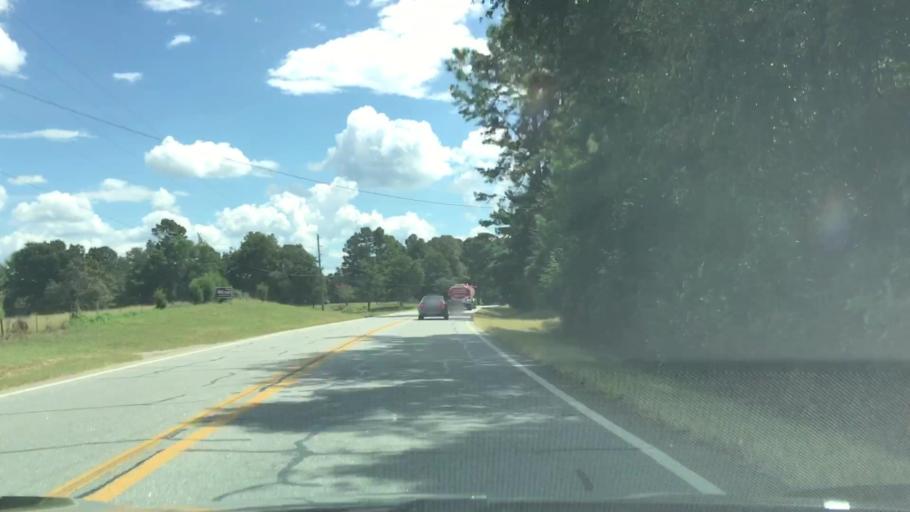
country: US
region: Georgia
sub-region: Oconee County
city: Watkinsville
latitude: 33.7814
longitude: -83.3122
